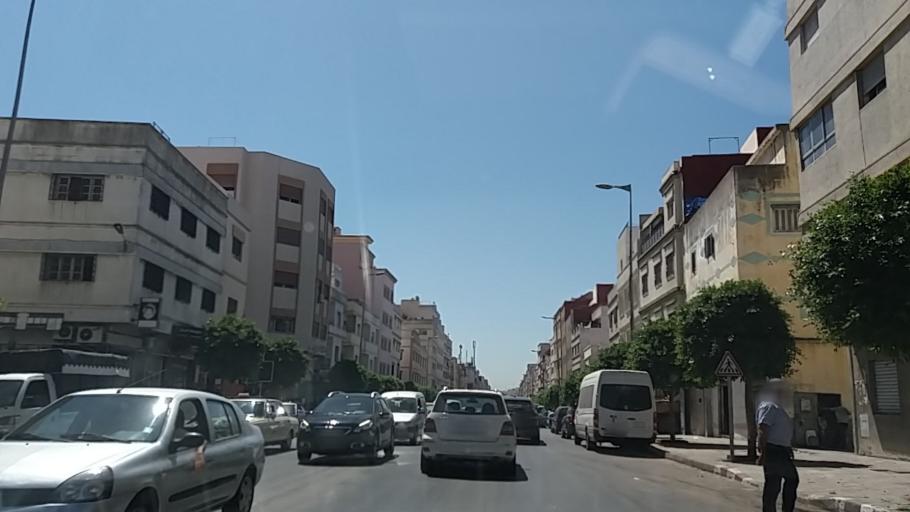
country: MA
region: Tanger-Tetouan
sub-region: Tanger-Assilah
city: Tangier
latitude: 35.7638
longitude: -5.8041
